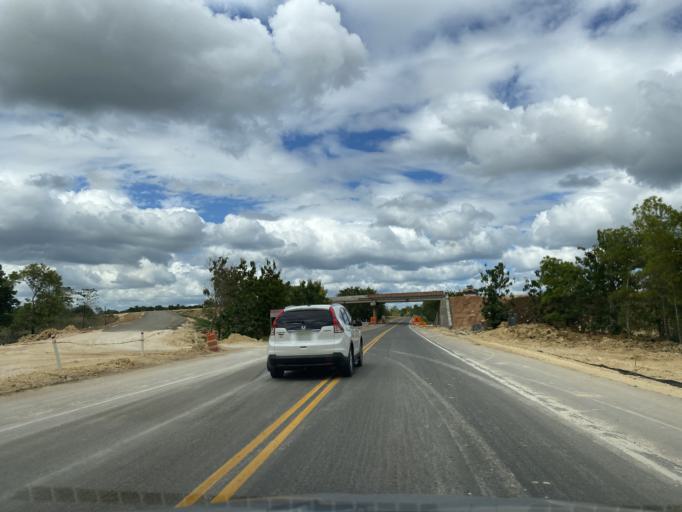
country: DO
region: Santo Domingo
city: Guerra
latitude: 18.5600
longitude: -69.7674
